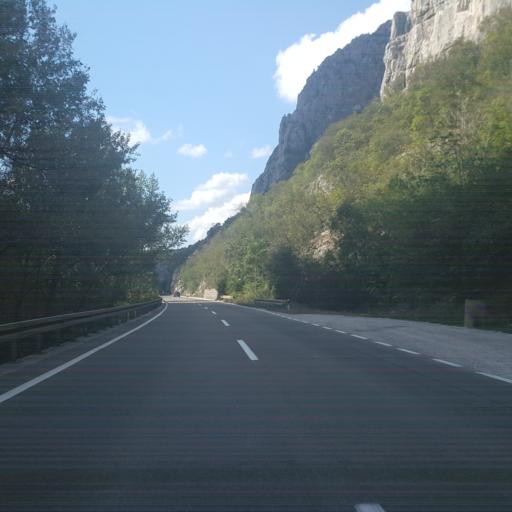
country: RS
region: Central Serbia
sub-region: Nisavski Okrug
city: Svrljig
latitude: 43.3321
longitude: 22.1508
